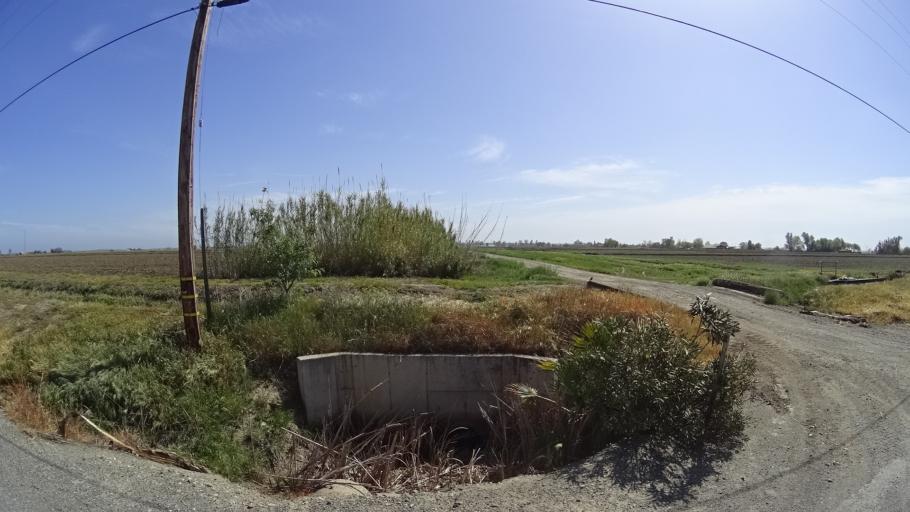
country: US
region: California
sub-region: Glenn County
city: Willows
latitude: 39.5871
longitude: -122.0557
